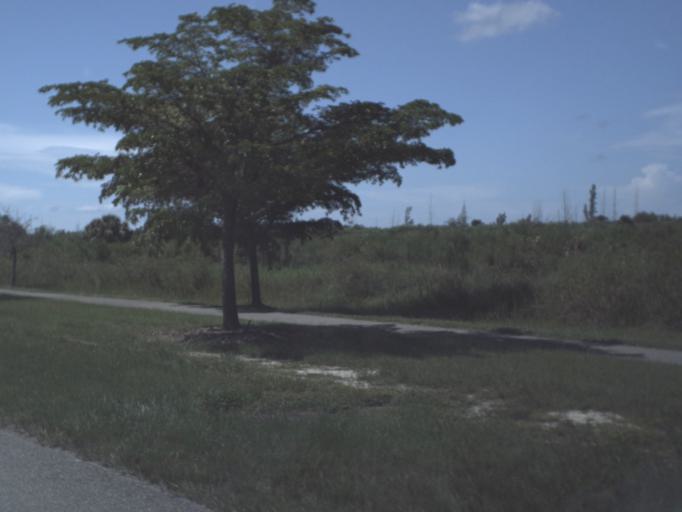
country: US
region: Florida
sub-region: Lee County
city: Pine Island Center
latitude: 26.6319
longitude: -82.0406
